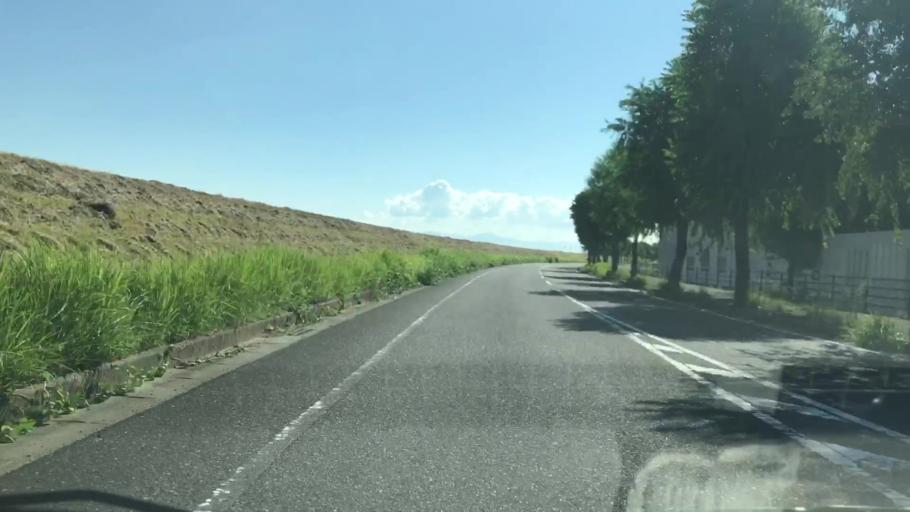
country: JP
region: Saga Prefecture
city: Okawa
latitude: 33.2297
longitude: 130.3757
